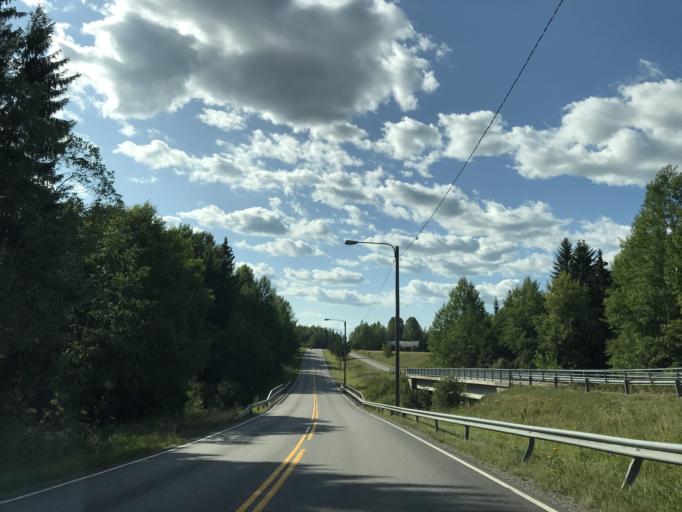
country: FI
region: Uusimaa
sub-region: Helsinki
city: Nurmijaervi
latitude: 60.4331
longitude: 24.8508
